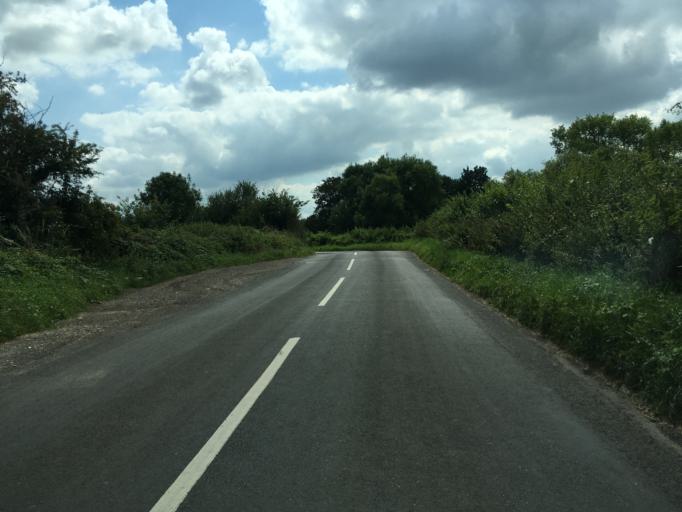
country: GB
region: England
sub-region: Gloucestershire
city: Gloucester
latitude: 51.8884
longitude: -2.2527
